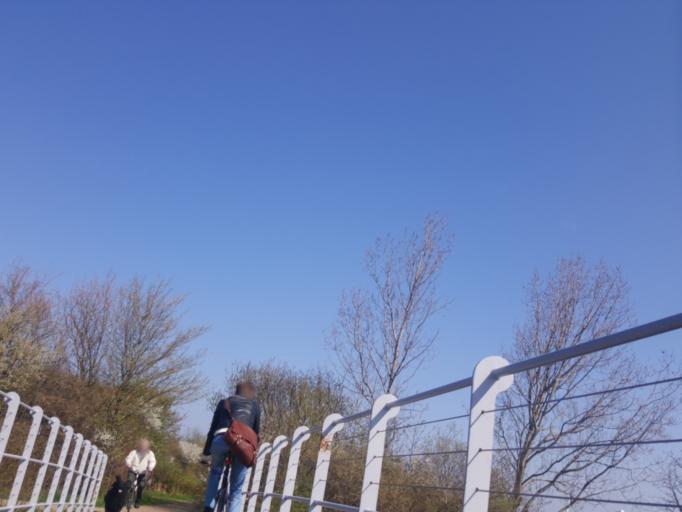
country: DK
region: Capital Region
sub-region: Hvidovre Kommune
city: Hvidovre
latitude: 55.6286
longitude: 12.5034
